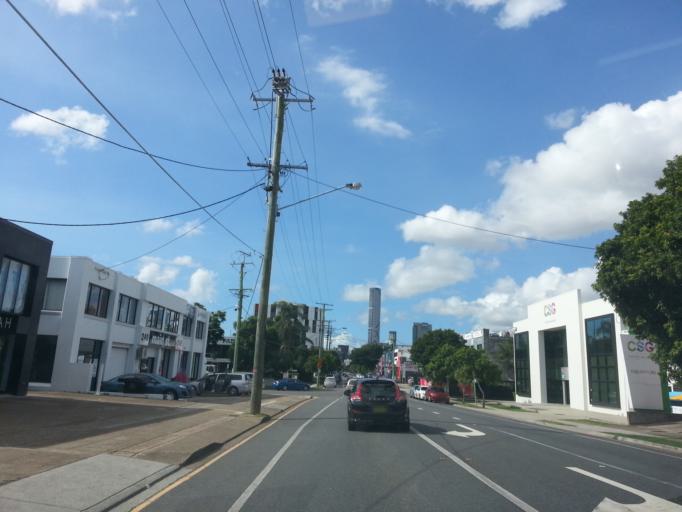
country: AU
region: Queensland
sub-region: Brisbane
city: Milton
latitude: -27.4782
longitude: 153.0066
